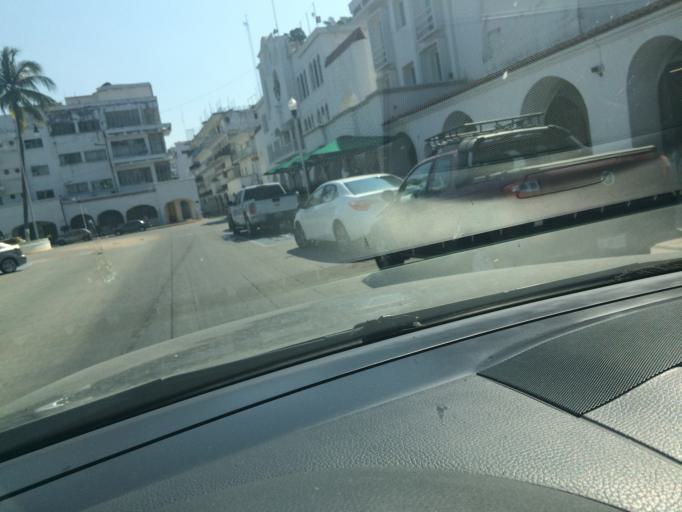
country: MX
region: Colima
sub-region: Manzanillo
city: Manzanillo
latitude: 19.0536
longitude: -104.3168
